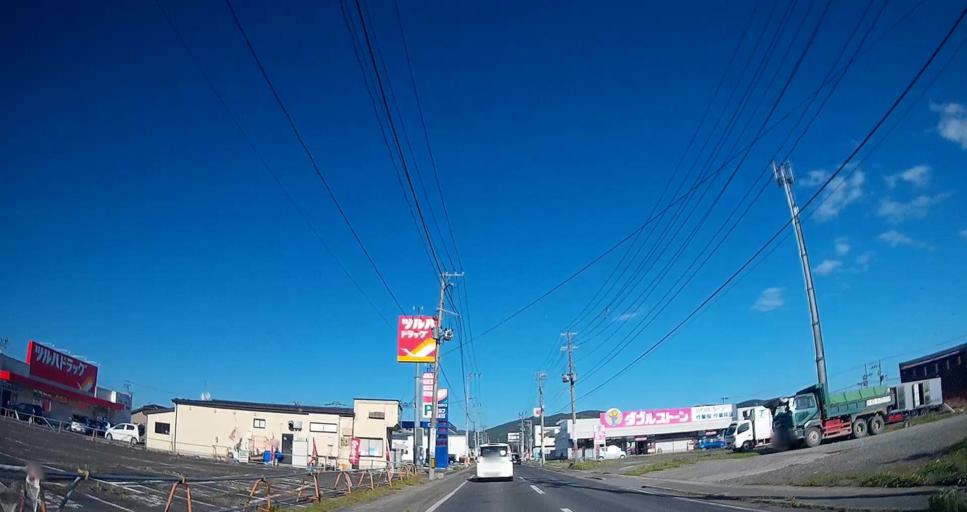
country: JP
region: Miyagi
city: Ishinomaki
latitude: 38.4178
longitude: 141.3434
